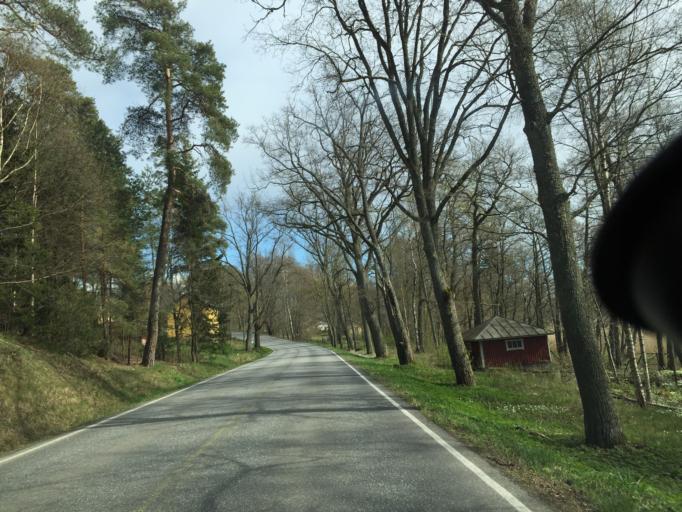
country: FI
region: Varsinais-Suomi
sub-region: Salo
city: Pernioe
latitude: 60.0341
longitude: 23.2103
